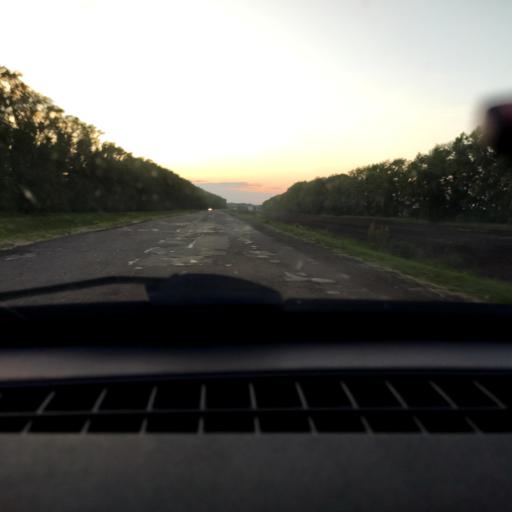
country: RU
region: Bashkortostan
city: Karmaskaly
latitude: 54.3890
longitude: 56.1755
